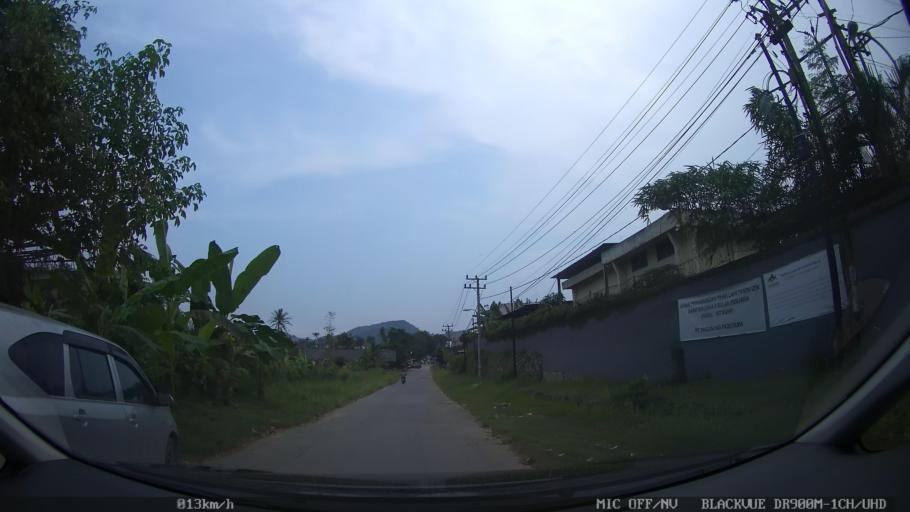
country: ID
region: Lampung
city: Panjang
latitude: -5.4342
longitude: 105.3269
